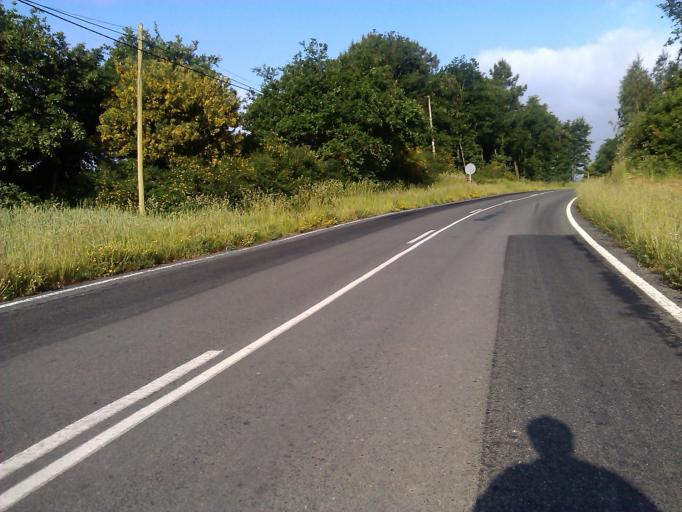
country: ES
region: Galicia
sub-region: Provincia da Coruna
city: Melide
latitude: 42.9056
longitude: -8.0430
